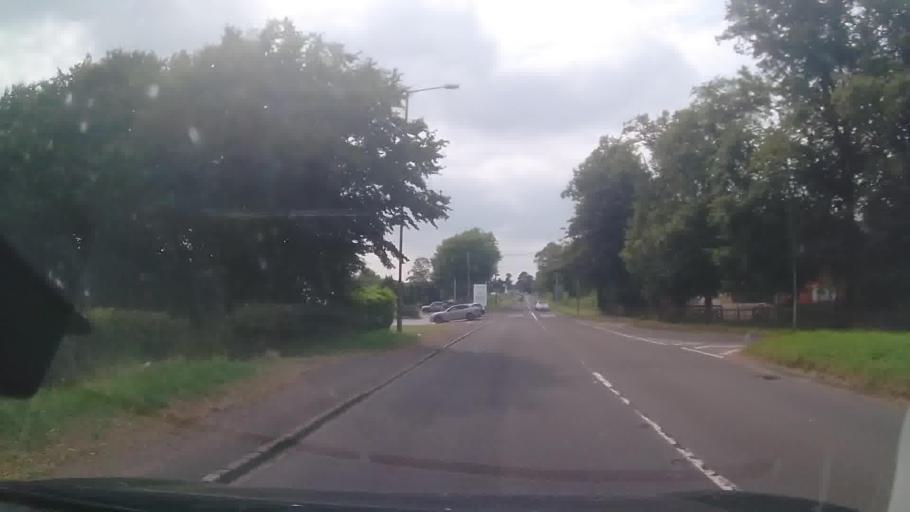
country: GB
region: England
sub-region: Staffordshire
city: Standon
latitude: 52.9460
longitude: -2.3380
